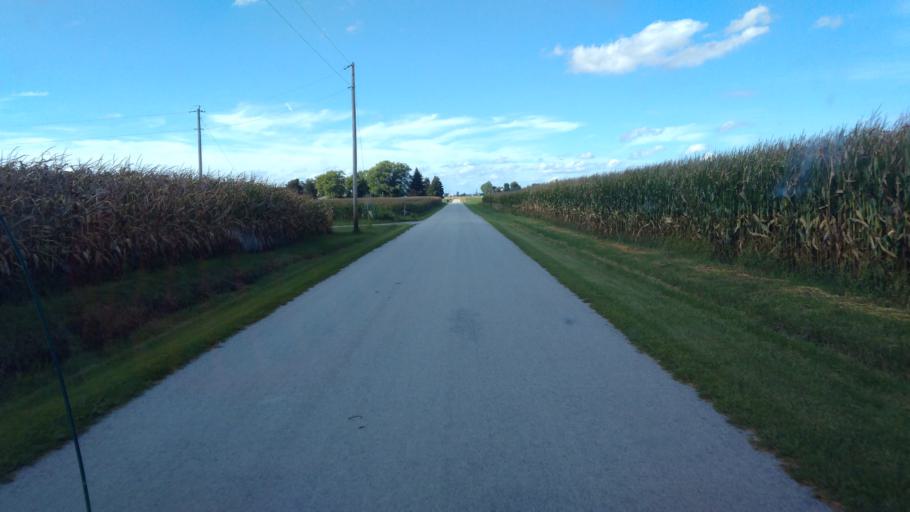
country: US
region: Ohio
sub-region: Hardin County
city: Kenton
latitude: 40.7259
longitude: -83.6723
